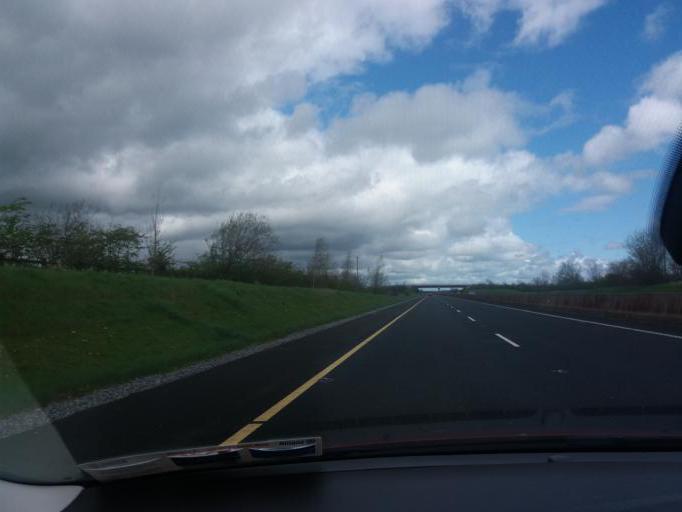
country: IE
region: Munster
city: Thurles
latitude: 52.6344
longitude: -7.7627
